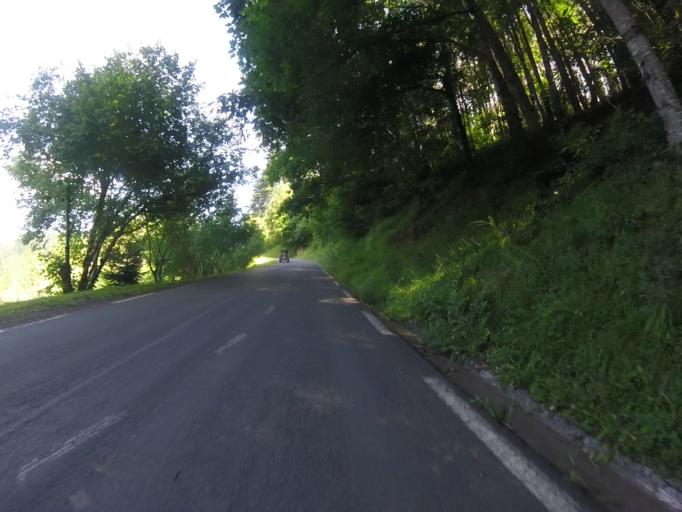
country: ES
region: Basque Country
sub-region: Provincia de Guipuzcoa
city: Beasain
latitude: 43.0770
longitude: -2.2223
